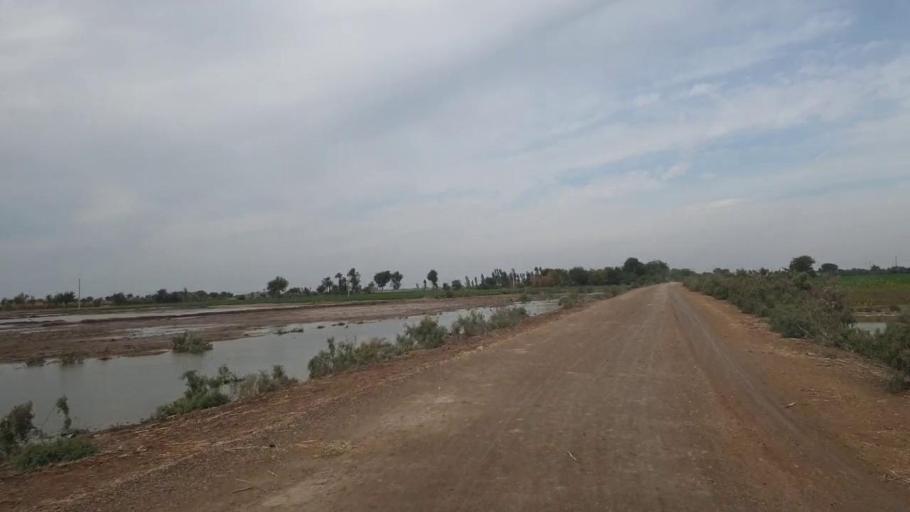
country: PK
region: Sindh
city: Sanghar
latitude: 26.0400
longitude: 68.9065
